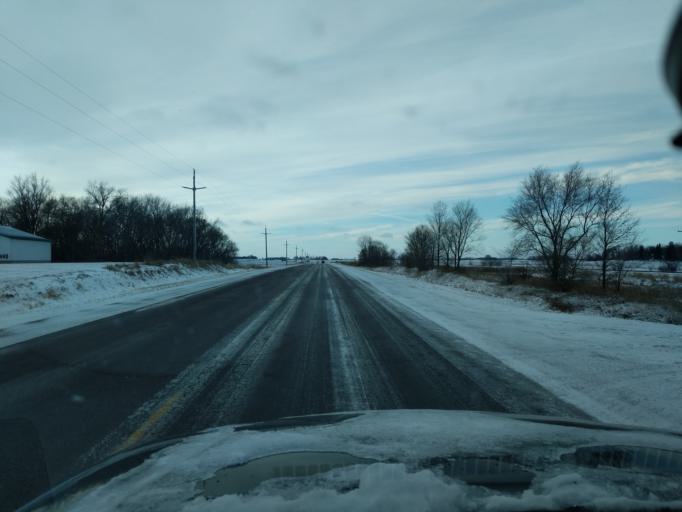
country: US
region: Minnesota
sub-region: Renville County
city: Hector
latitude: 44.7246
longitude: -94.5385
